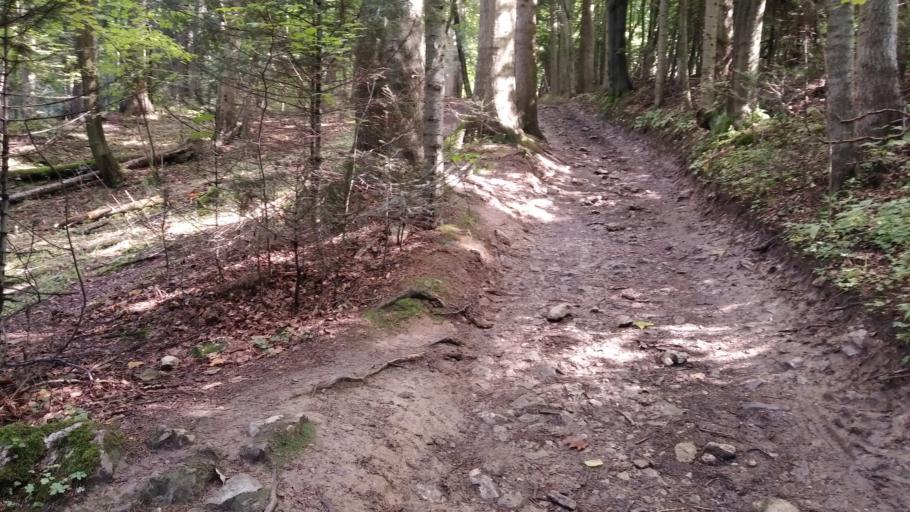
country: PL
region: Lesser Poland Voivodeship
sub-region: Powiat nowotarski
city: Kroscienko nad Dunajcem
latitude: 49.4260
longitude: 20.4252
